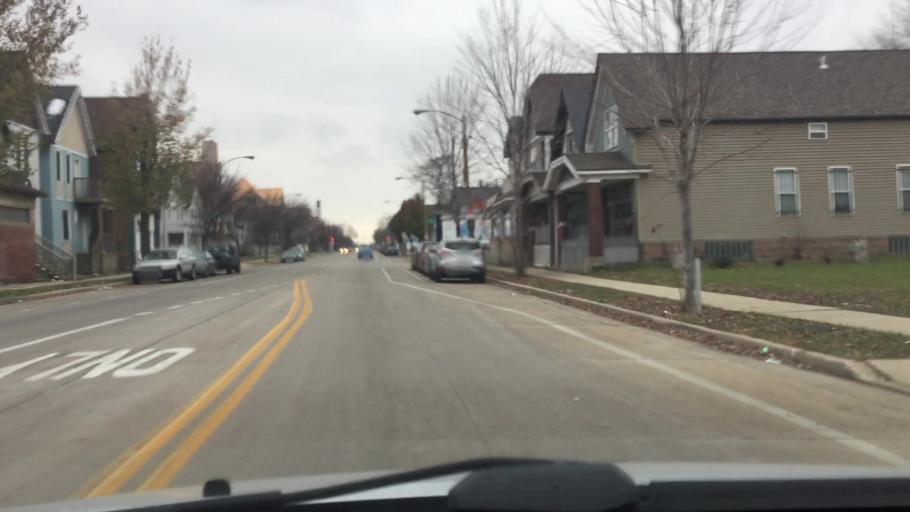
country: US
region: Wisconsin
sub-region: Milwaukee County
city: Milwaukee
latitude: 43.0433
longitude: -87.9345
